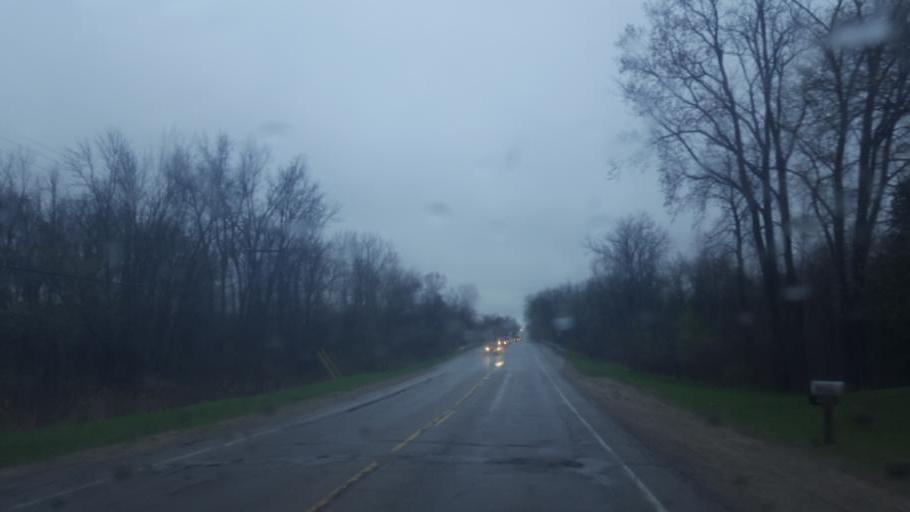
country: US
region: Michigan
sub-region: Isabella County
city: Mount Pleasant
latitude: 43.6234
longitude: -84.7680
